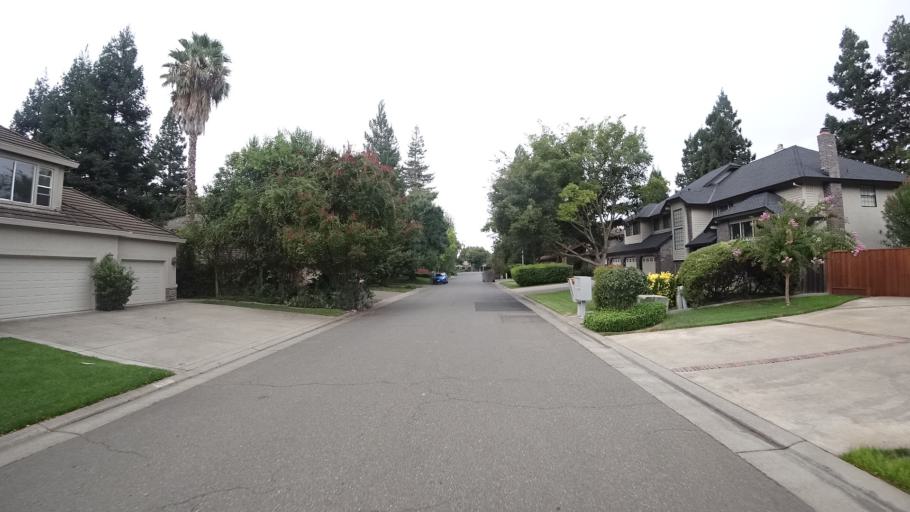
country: US
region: California
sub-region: Sacramento County
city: Laguna
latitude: 38.4147
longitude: -121.4477
